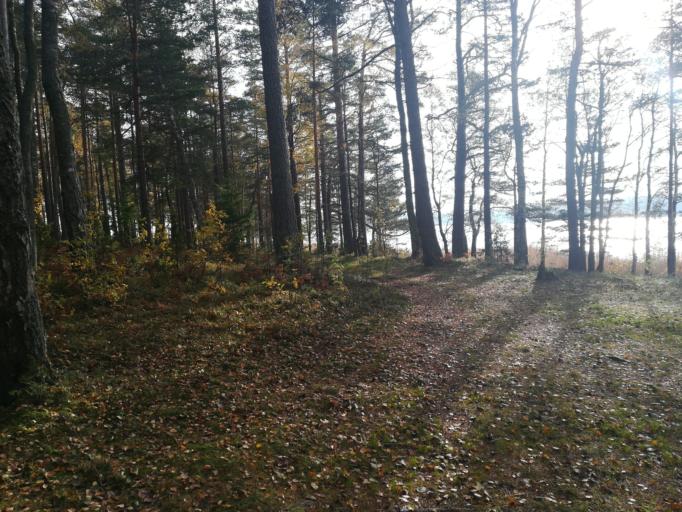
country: RU
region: Leningrad
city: Ust'-Luga
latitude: 59.7524
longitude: 28.1498
